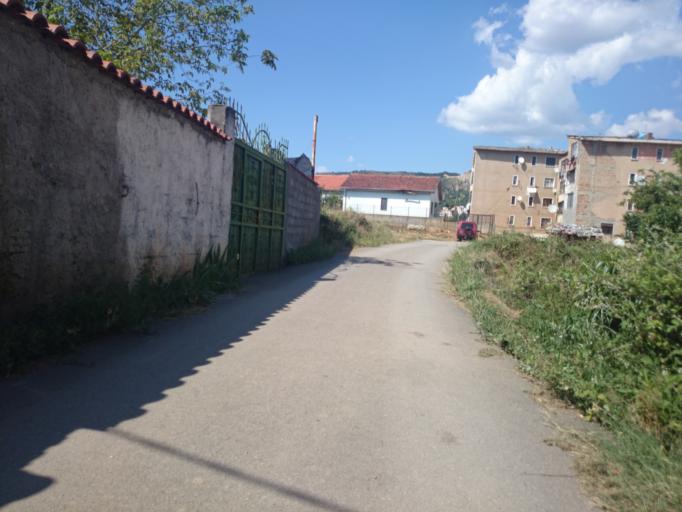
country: AL
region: Diber
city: Peshkopi
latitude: 41.6819
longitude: 20.4253
